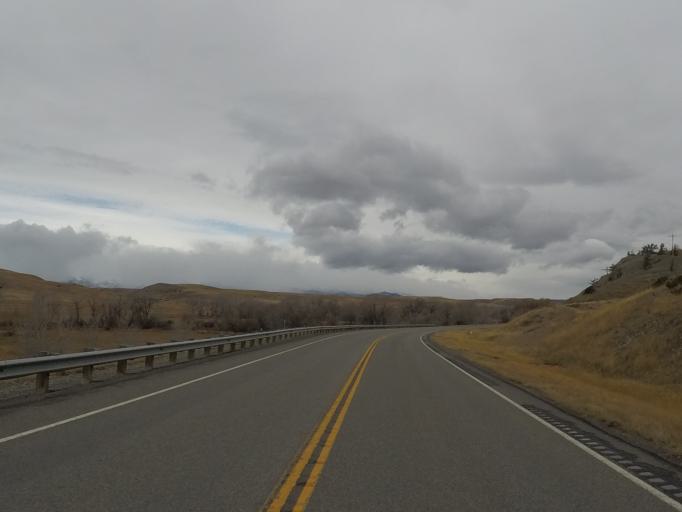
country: US
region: Montana
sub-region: Sweet Grass County
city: Big Timber
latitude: 45.9039
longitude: -109.9762
